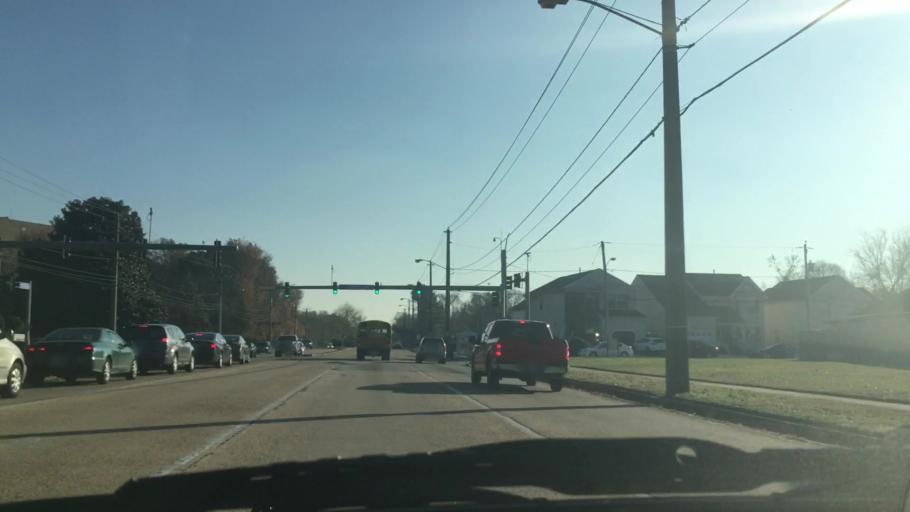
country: US
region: Virginia
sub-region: City of Norfolk
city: Norfolk
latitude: 36.9082
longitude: -76.2405
